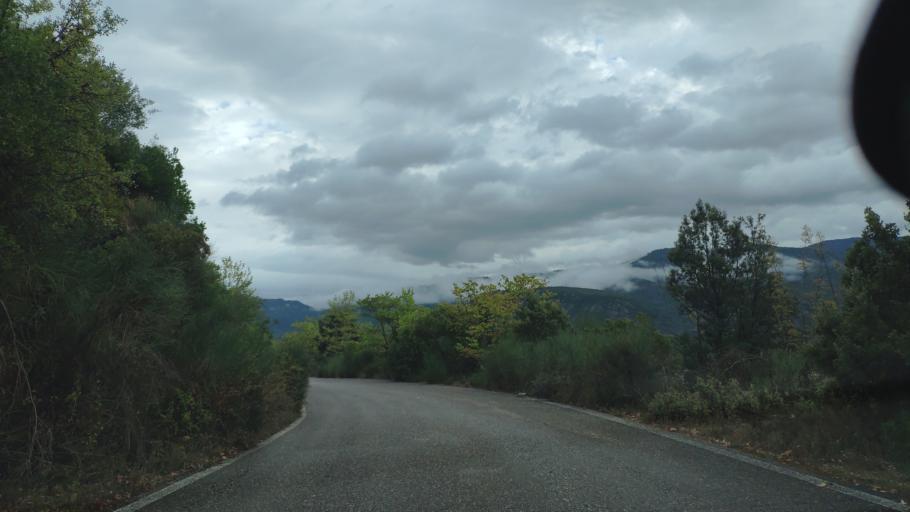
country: GR
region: West Greece
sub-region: Nomos Aitolias kai Akarnanias
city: Sardinia
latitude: 38.8488
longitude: 21.3275
